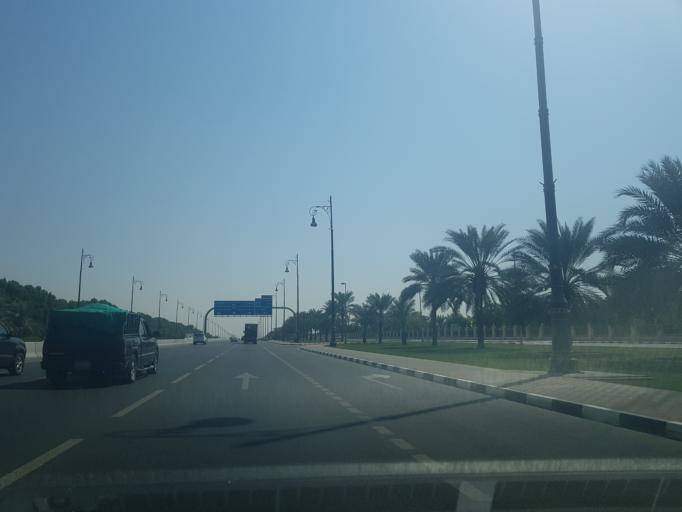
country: AE
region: Ash Shariqah
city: Sharjah
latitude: 25.3156
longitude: 55.5316
